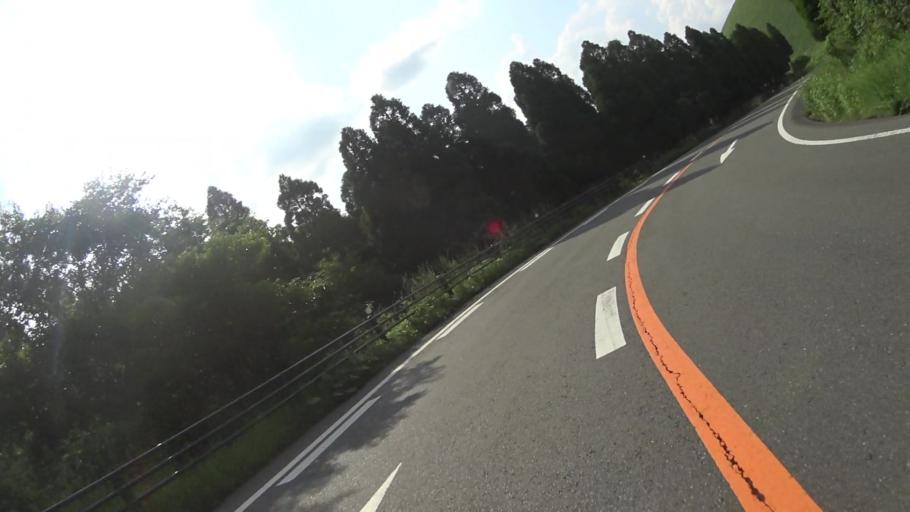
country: JP
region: Kumamoto
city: Aso
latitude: 32.9003
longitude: 131.0457
